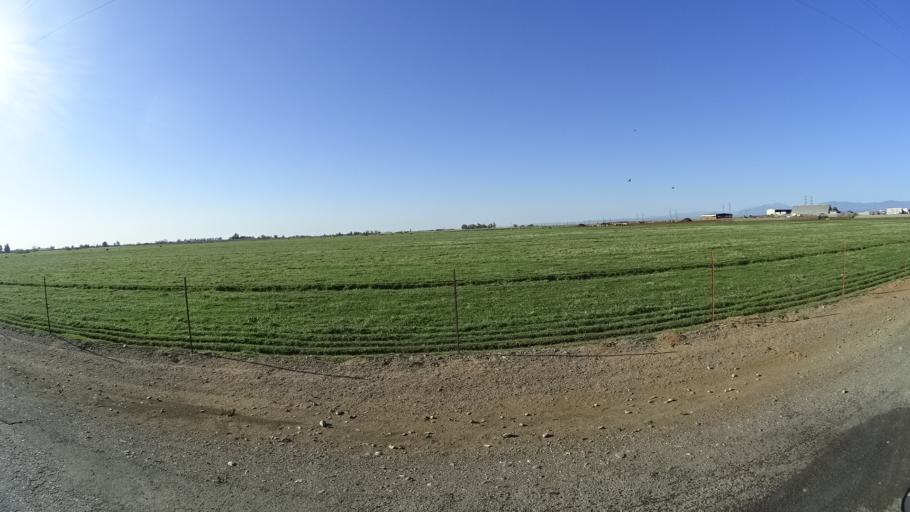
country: US
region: California
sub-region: Glenn County
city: Orland
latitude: 39.7590
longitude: -122.2582
